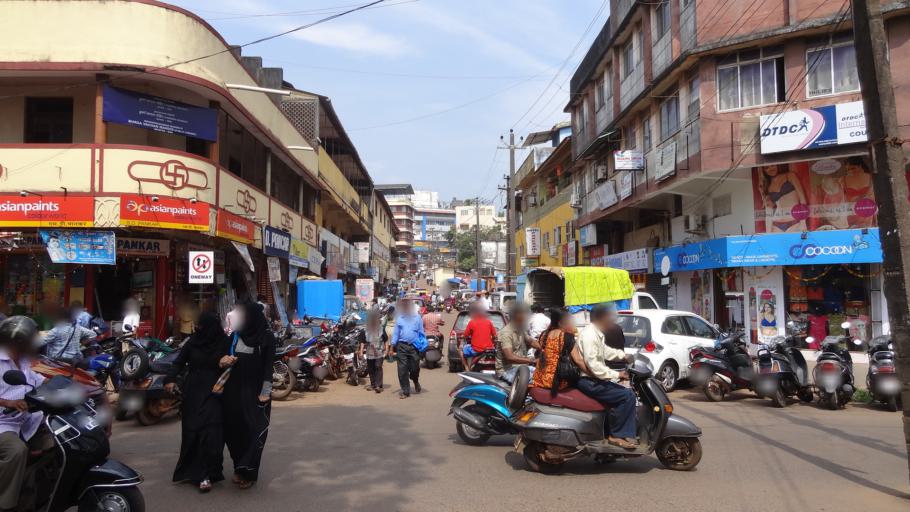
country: IN
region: Goa
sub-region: North Goa
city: Mapuca
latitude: 15.5894
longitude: 73.8118
